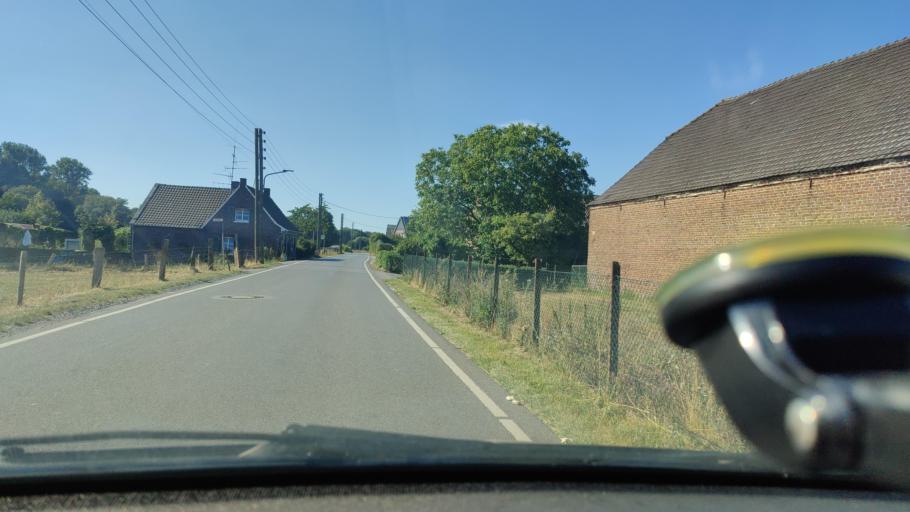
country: DE
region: North Rhine-Westphalia
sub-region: Regierungsbezirk Dusseldorf
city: Wachtendonk
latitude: 51.4446
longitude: 6.3851
